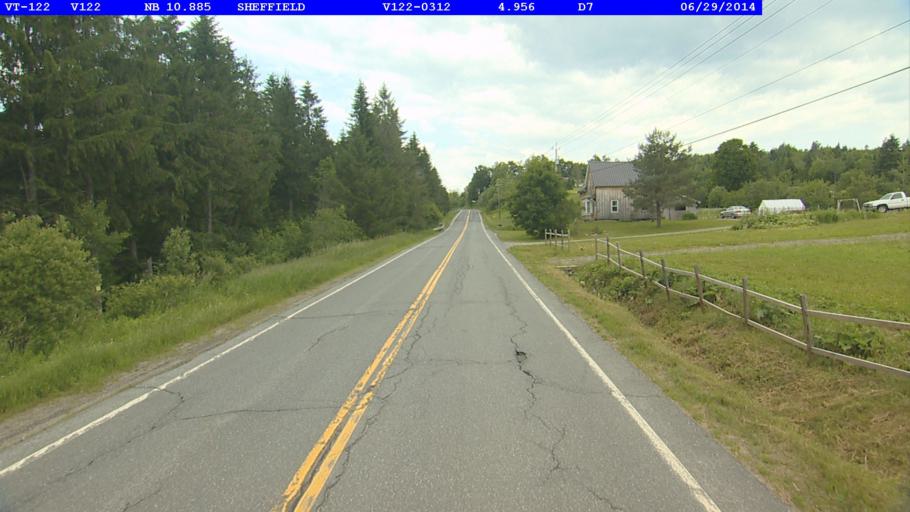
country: US
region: Vermont
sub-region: Caledonia County
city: Lyndonville
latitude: 44.6415
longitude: -72.1540
